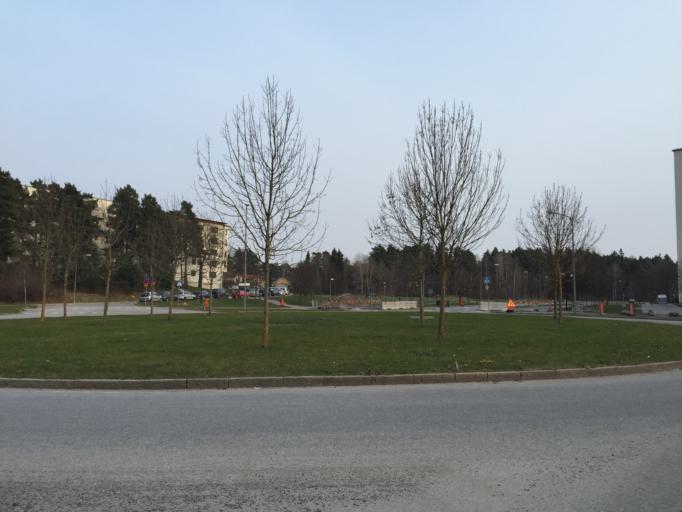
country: SE
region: Stockholm
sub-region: Stockholms Kommun
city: Bromma
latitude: 59.3558
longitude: 17.8871
